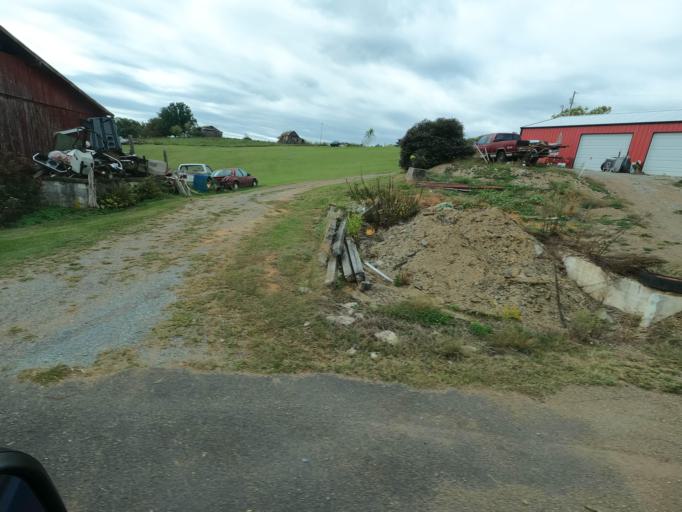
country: US
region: Tennessee
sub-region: Washington County
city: Jonesborough
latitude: 36.2531
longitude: -82.5421
